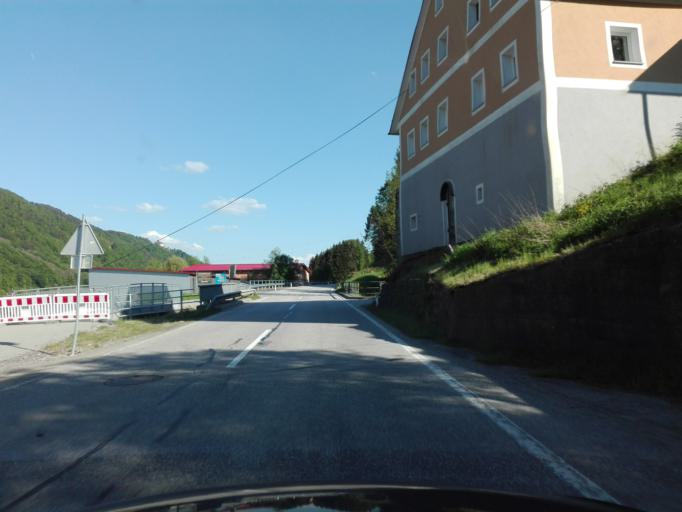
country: AT
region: Upper Austria
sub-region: Politischer Bezirk Rohrbach
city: Pfarrkirchen im Muehlkreis
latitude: 48.4907
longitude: 13.7428
